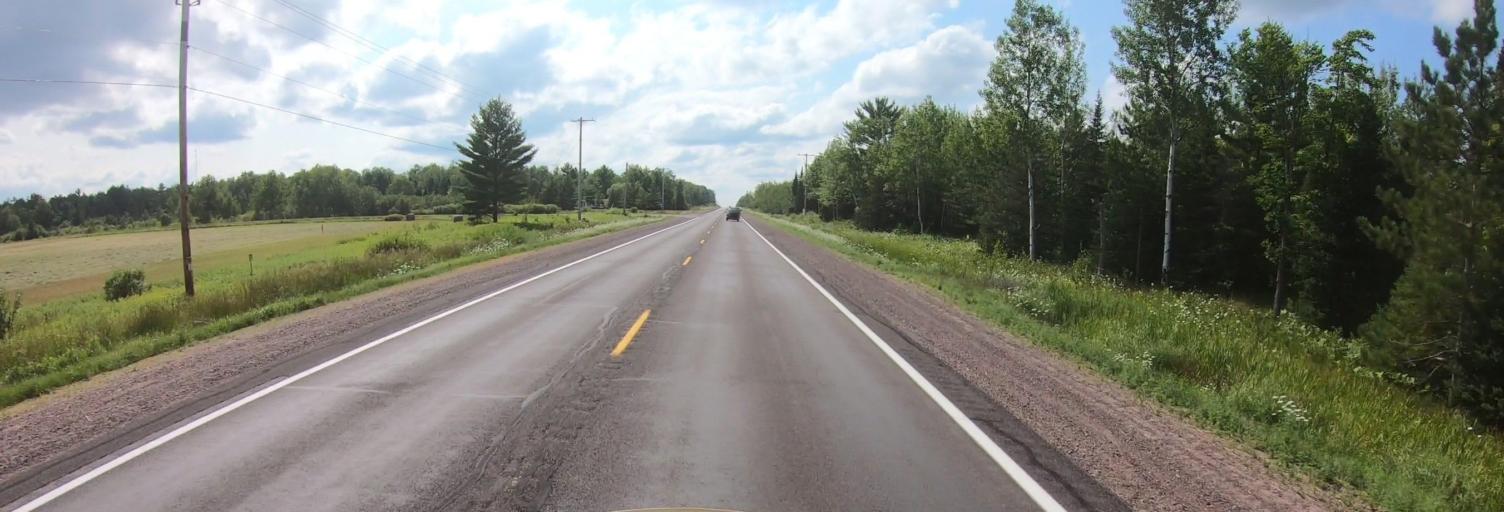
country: US
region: Michigan
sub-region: Ontonagon County
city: Ontonagon
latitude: 46.5348
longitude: -89.2388
